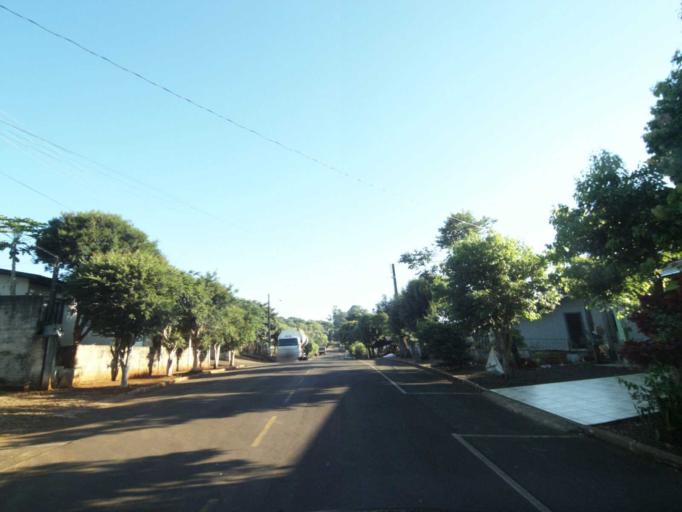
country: BR
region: Parana
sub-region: Coronel Vivida
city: Coronel Vivida
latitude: -25.9692
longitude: -52.8121
